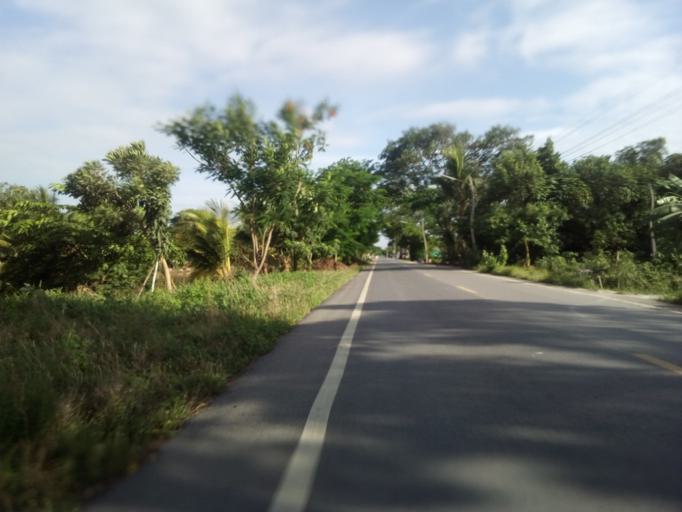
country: TH
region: Pathum Thani
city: Nong Suea
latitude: 14.1068
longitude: 100.8461
